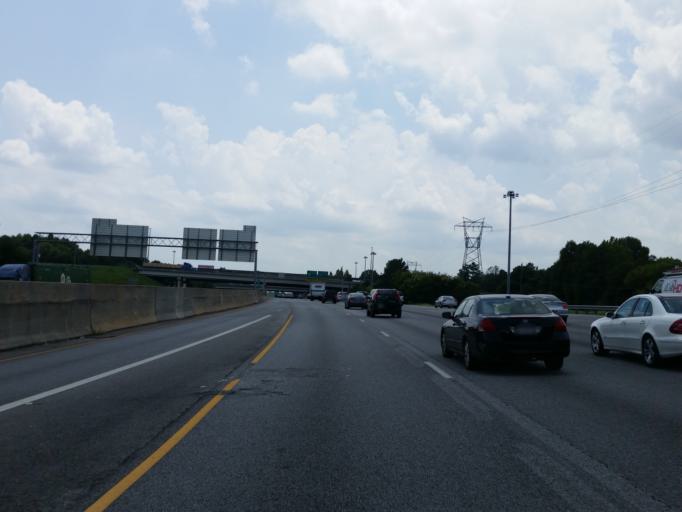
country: US
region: Georgia
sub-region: Fulton County
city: Hapeville
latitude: 33.6366
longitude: -84.4015
